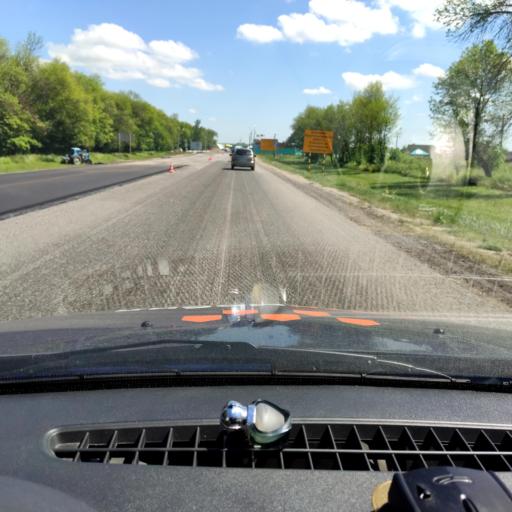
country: RU
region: Orjol
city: Zmiyevka
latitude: 52.7054
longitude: 36.3648
